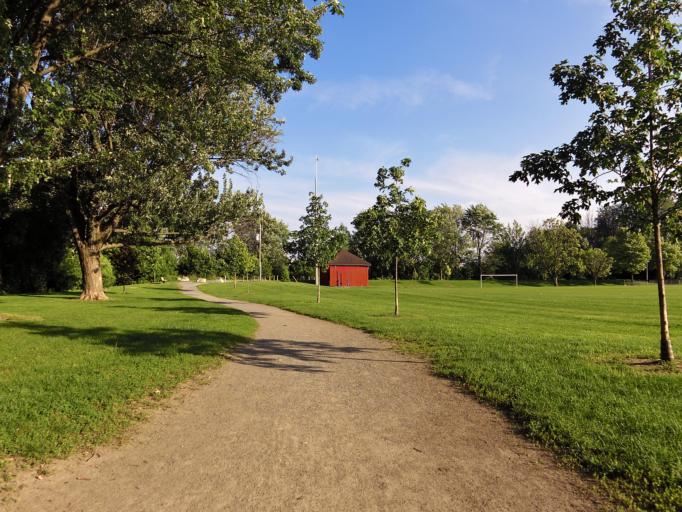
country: CA
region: Ontario
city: Ottawa
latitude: 45.3881
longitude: -75.6875
